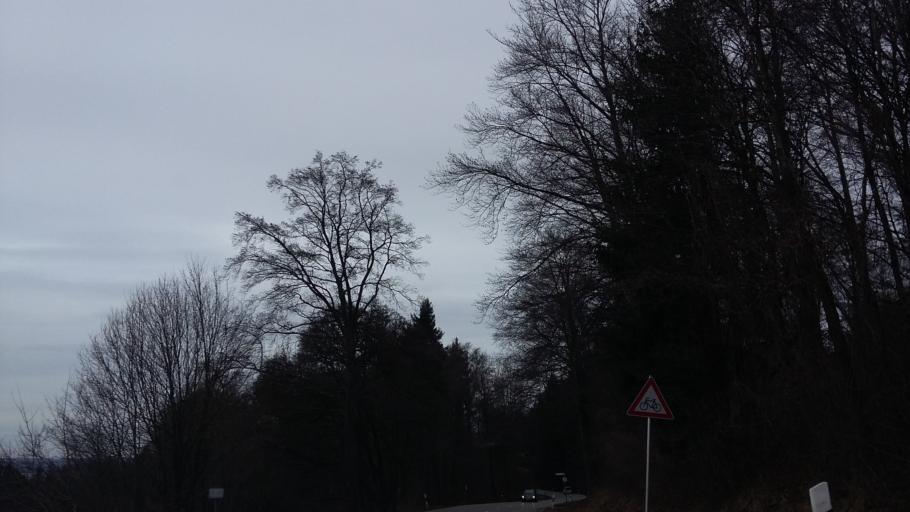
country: DE
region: Bavaria
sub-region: Upper Bavaria
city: Andechs
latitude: 47.9654
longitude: 11.1746
